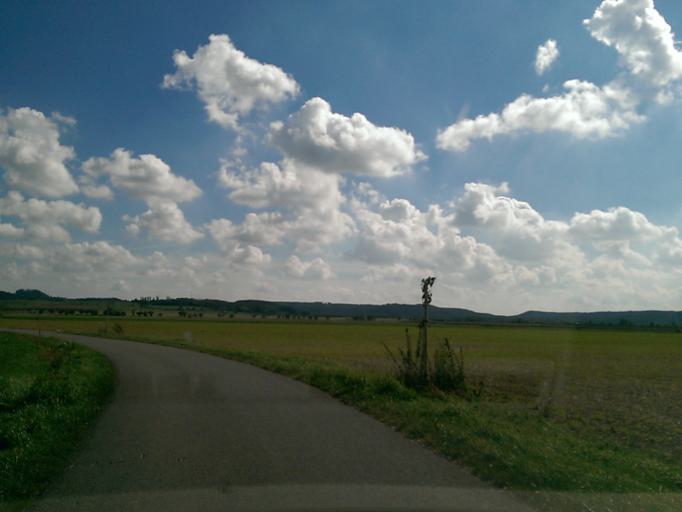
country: CZ
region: Central Bohemia
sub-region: Okres Mlada Boleslav
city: Zd'ar
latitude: 50.5582
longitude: 15.0838
